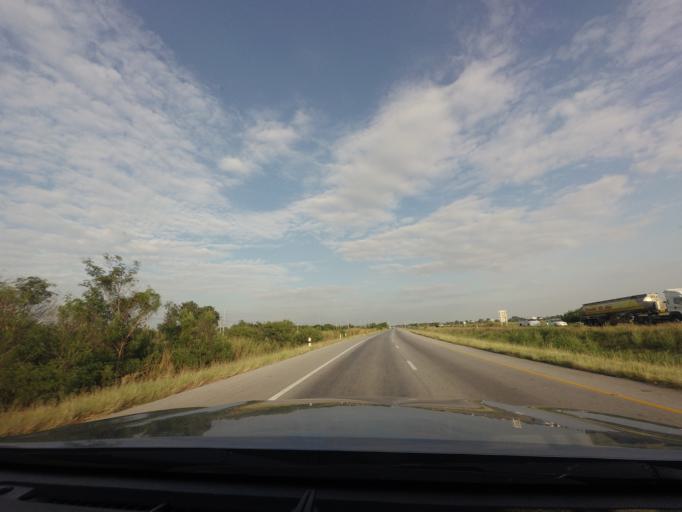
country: TH
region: Nakhon Sawan
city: Nakhon Sawan
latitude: 15.7683
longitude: 100.1094
